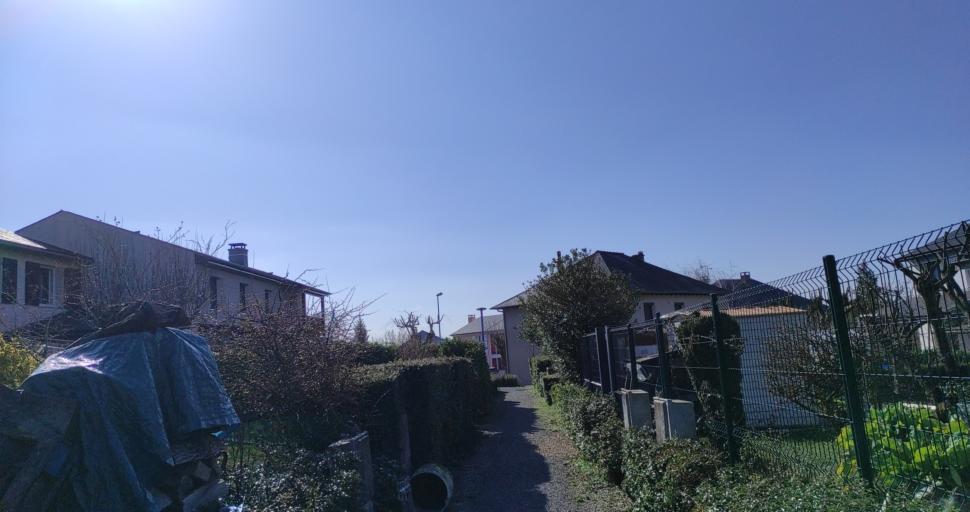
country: FR
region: Midi-Pyrenees
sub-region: Departement de l'Aveyron
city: Rodez
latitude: 44.3781
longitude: 2.5739
